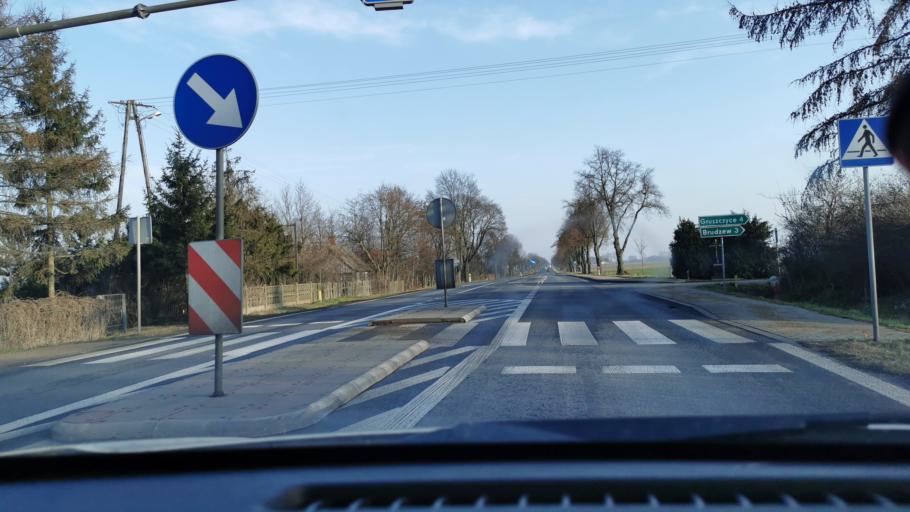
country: PL
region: Lodz Voivodeship
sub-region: Powiat sieradzki
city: Blaszki
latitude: 51.6405
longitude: 18.5015
